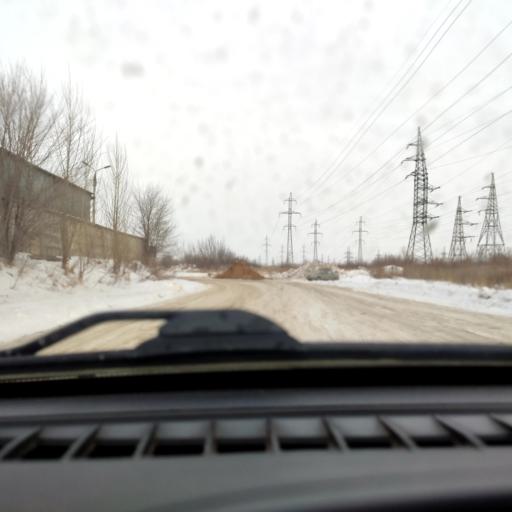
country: RU
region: Samara
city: Tol'yatti
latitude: 53.5851
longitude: 49.2655
